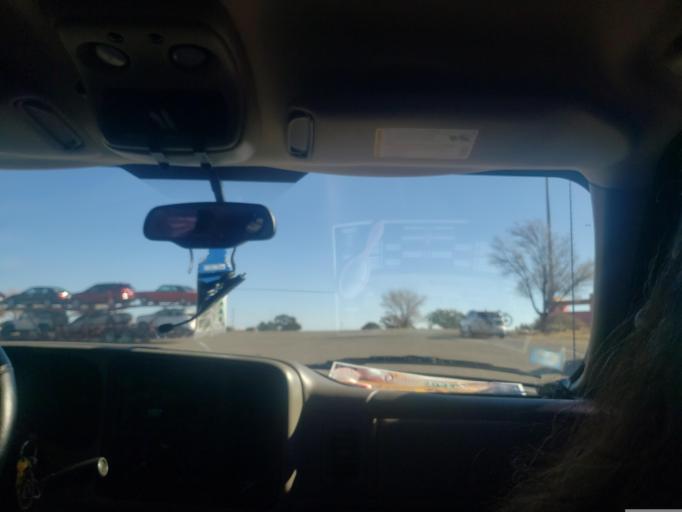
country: US
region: New Mexico
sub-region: Guadalupe County
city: Santa Rosa
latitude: 34.9802
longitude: -105.0852
